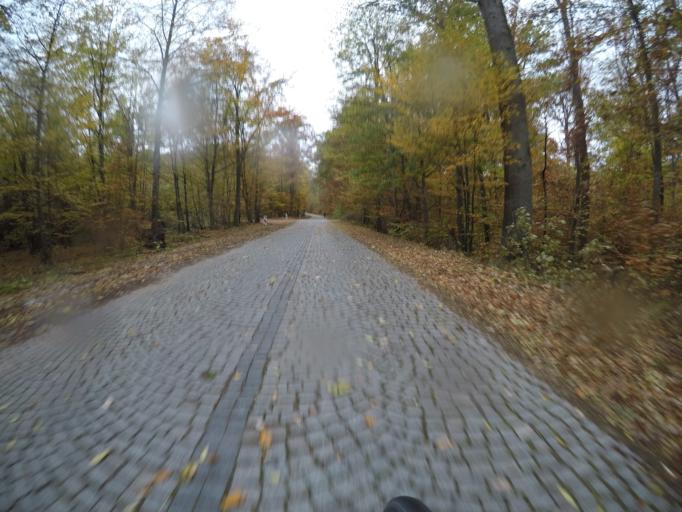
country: DE
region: Baden-Wuerttemberg
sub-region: Regierungsbezirk Stuttgart
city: Schonaich
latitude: 48.6993
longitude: 9.0691
